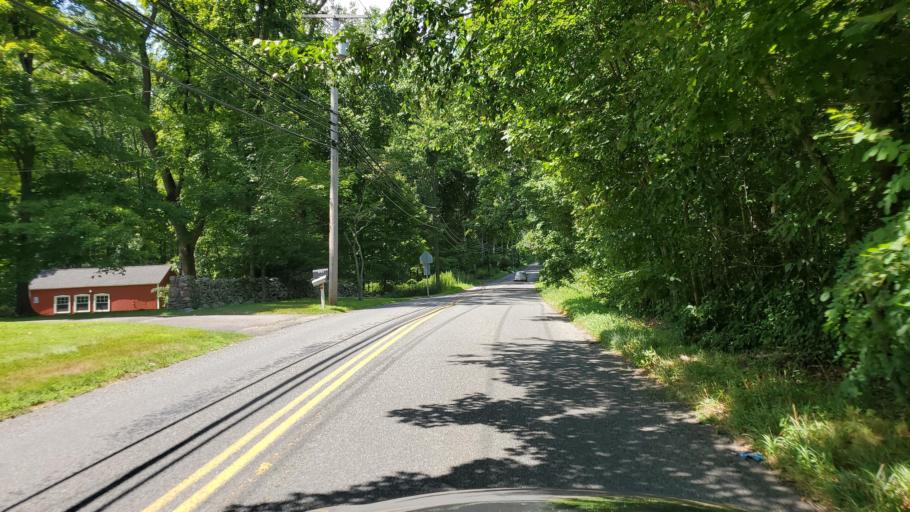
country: US
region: Connecticut
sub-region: Fairfield County
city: Southport
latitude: 41.1826
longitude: -73.3053
